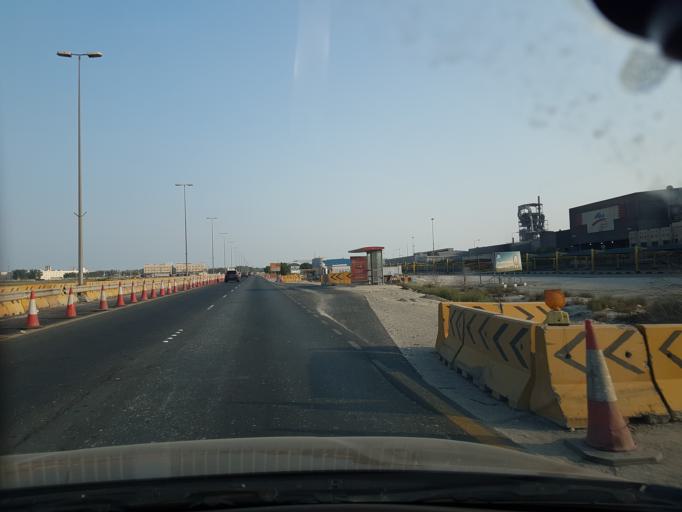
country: BH
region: Northern
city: Sitrah
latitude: 26.0919
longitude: 50.6096
